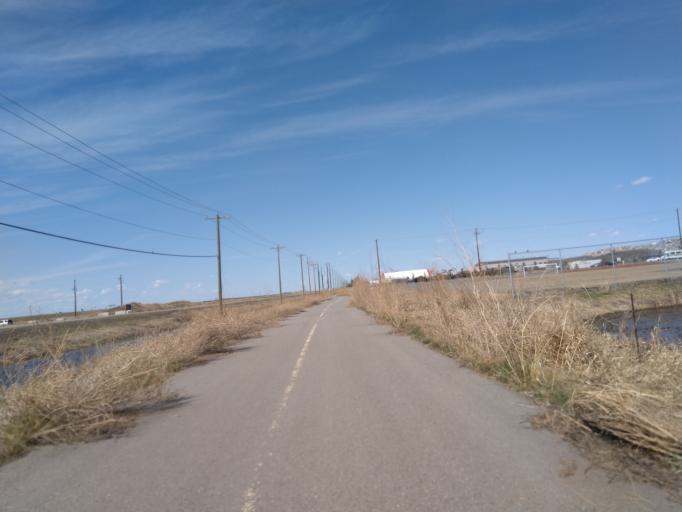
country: CA
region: Alberta
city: Chestermere
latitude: 50.9608
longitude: -113.9114
